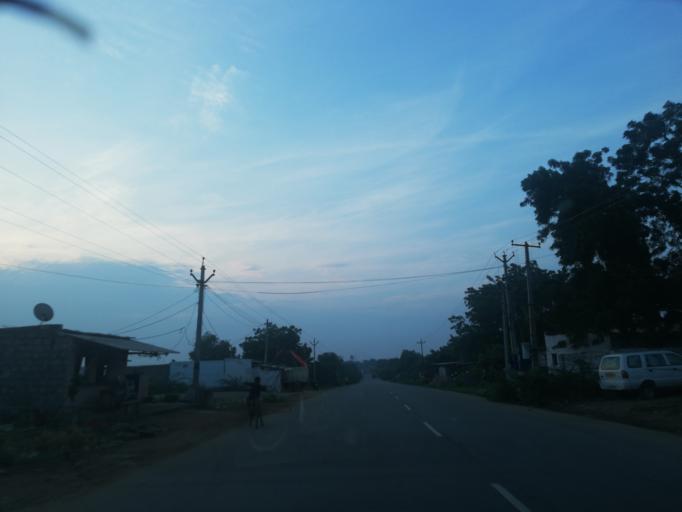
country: IN
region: Andhra Pradesh
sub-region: Guntur
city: Macherla
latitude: 16.5913
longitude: 79.3170
